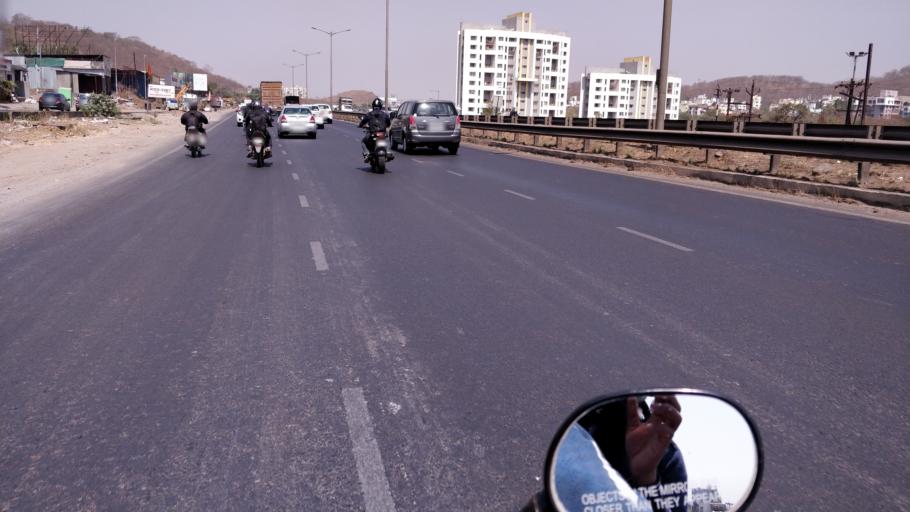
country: IN
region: Maharashtra
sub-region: Pune Division
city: Shivaji Nagar
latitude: 18.5404
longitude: 73.7797
